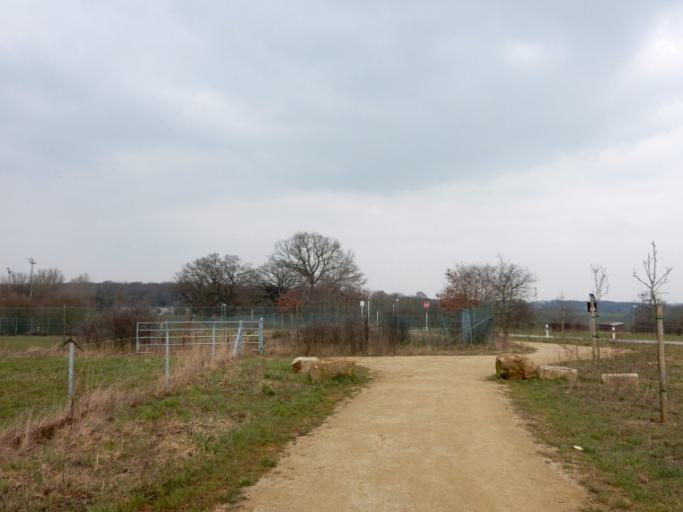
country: LU
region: Luxembourg
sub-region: Canton d'Esch-sur-Alzette
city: Mondercange
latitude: 49.5427
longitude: 5.9779
